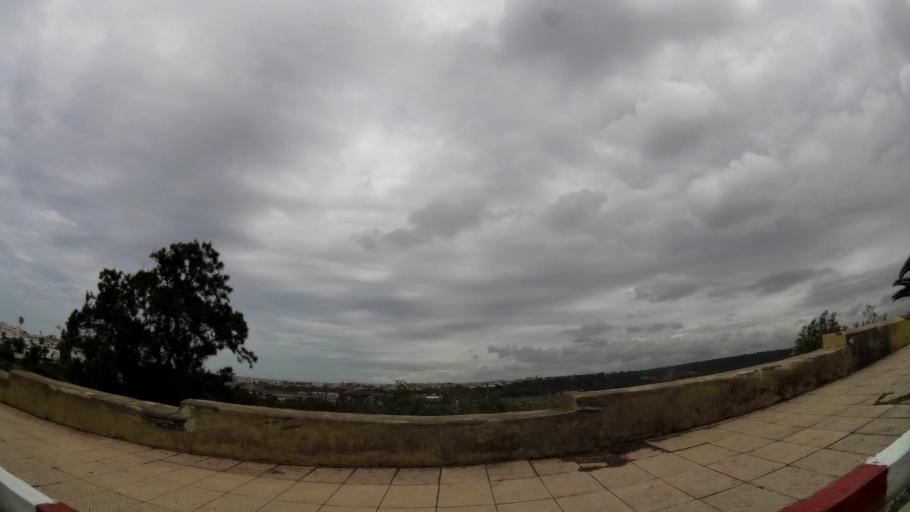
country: MA
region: Rabat-Sale-Zemmour-Zaer
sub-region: Rabat
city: Rabat
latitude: 34.0157
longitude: -6.8203
